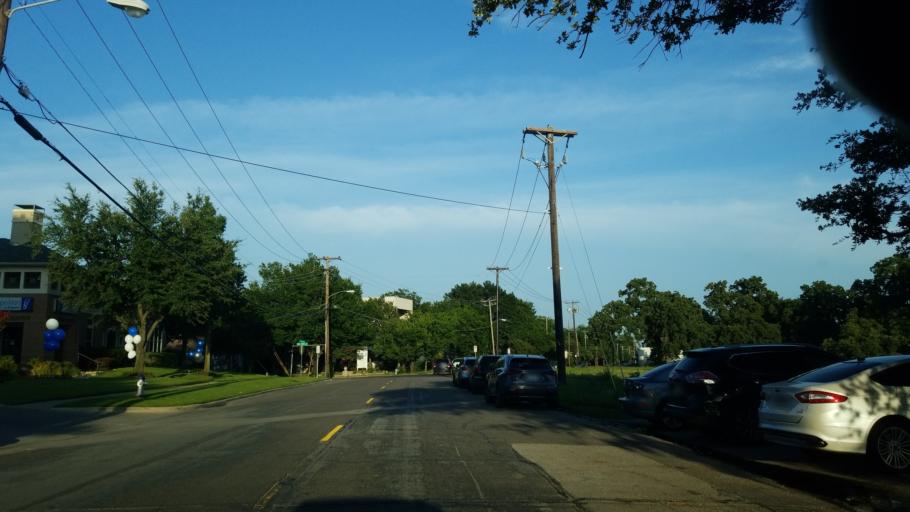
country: US
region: Texas
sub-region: Dallas County
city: Highland Park
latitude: 32.8107
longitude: -96.7899
